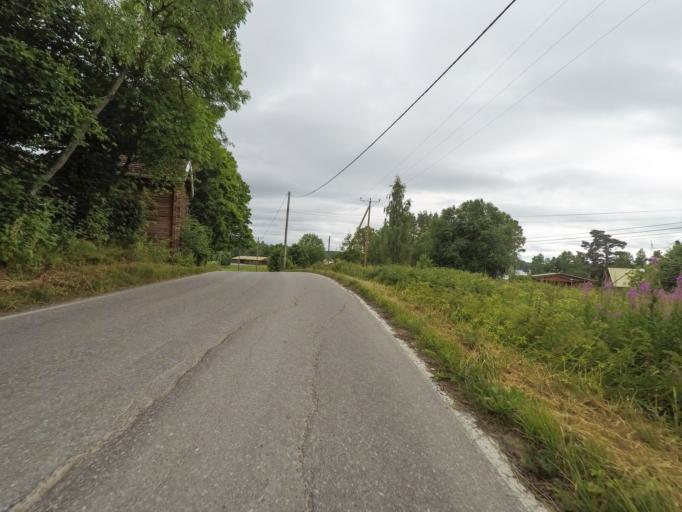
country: FI
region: Uusimaa
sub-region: Helsinki
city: Karjalohja
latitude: 60.2621
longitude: 23.7109
